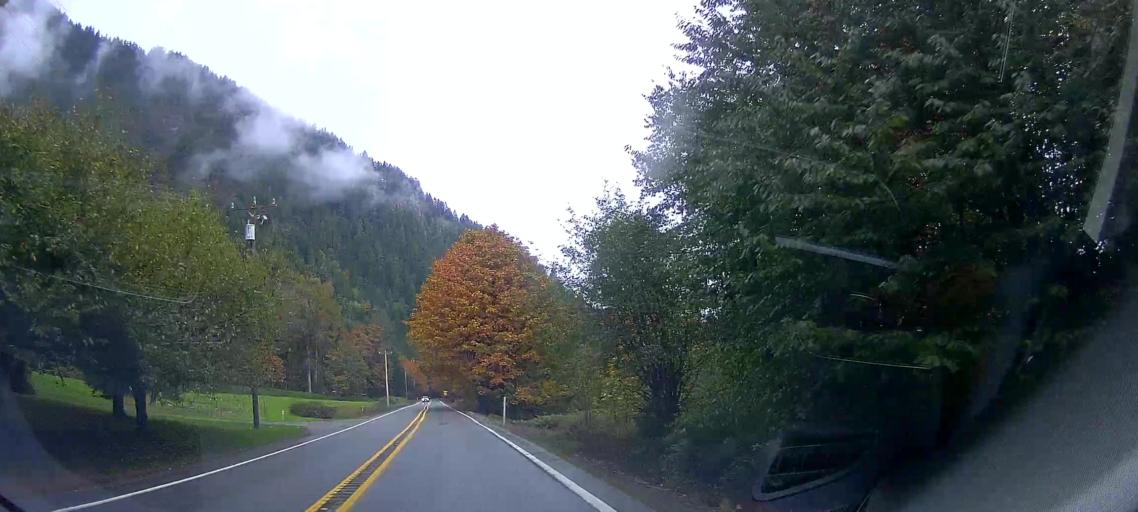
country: US
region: Washington
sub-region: Snohomish County
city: Darrington
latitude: 48.4892
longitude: -121.5781
